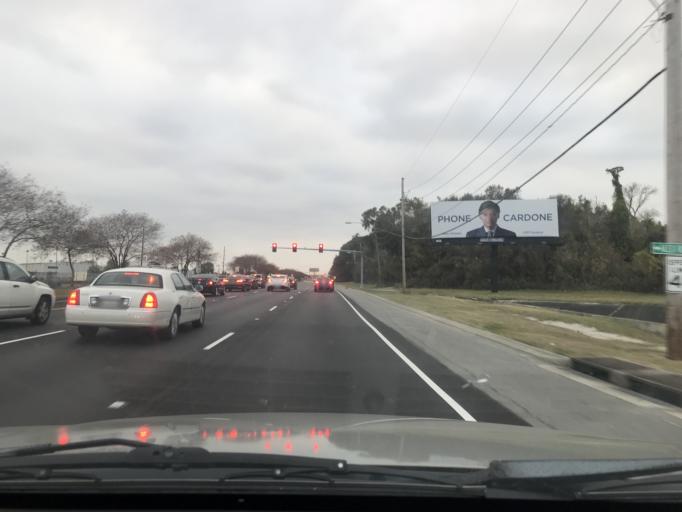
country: US
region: Louisiana
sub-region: Jefferson Parish
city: Woodmere
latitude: 29.8701
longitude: -90.0765
